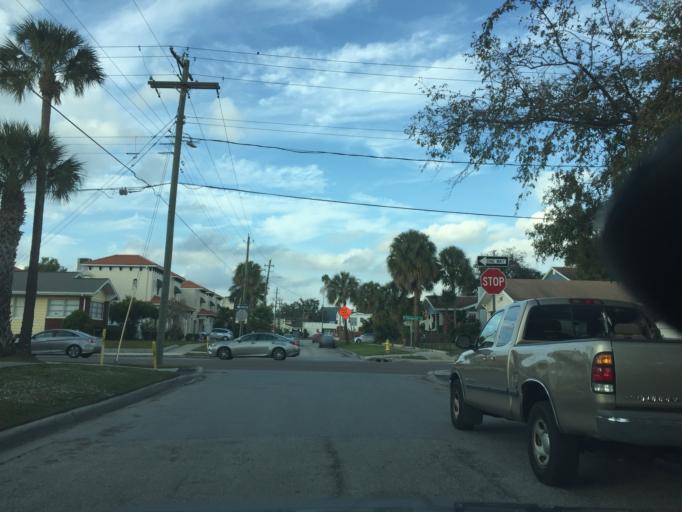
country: US
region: Florida
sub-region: Hillsborough County
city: Tampa
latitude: 27.9431
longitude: -82.4799
